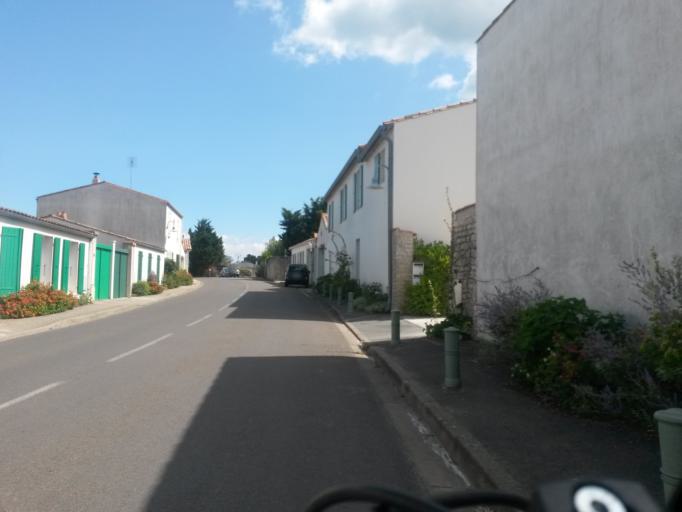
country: FR
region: Poitou-Charentes
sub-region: Departement de la Charente-Maritime
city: La Flotte
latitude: 46.1849
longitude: -1.3173
